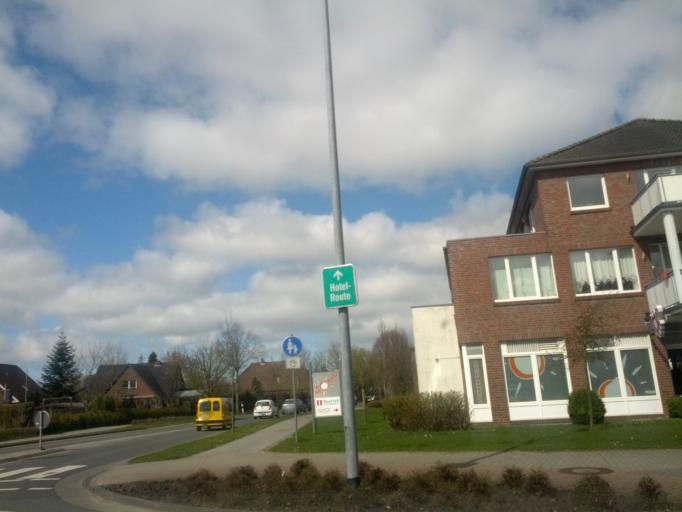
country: DE
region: Lower Saxony
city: Esens
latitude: 53.6449
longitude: 7.6080
